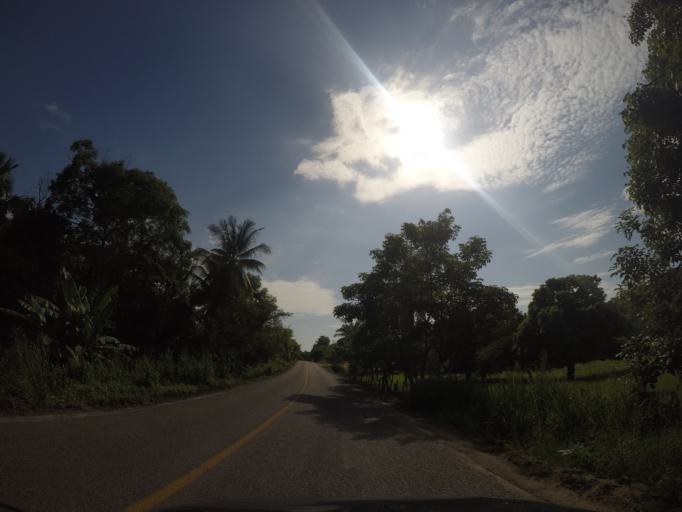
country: MX
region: Oaxaca
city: San Pedro Mixtepec
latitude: 15.9399
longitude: -97.1605
